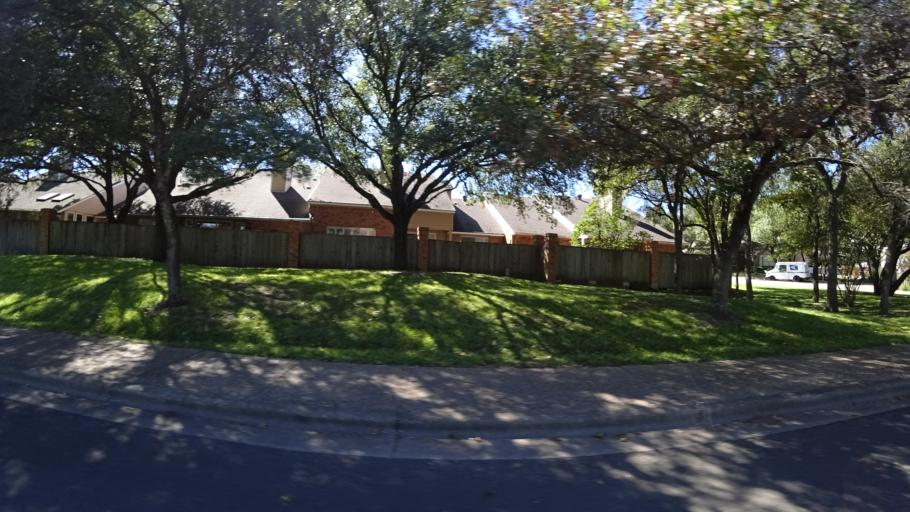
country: US
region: Texas
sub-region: Williamson County
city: Jollyville
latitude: 30.3676
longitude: -97.7539
